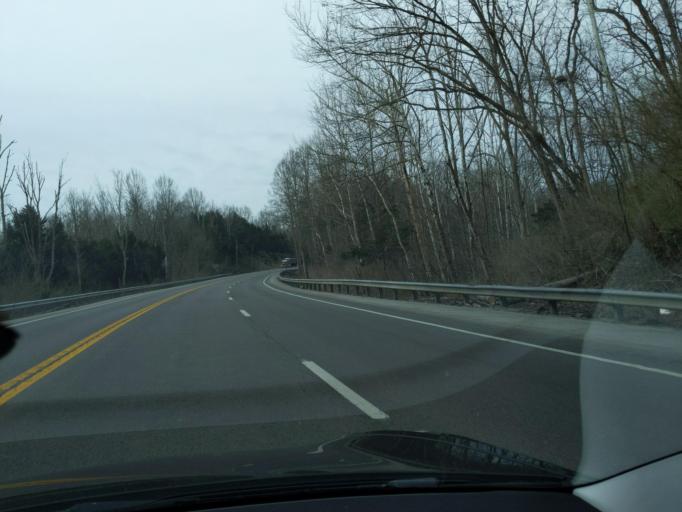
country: US
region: Kentucky
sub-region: Clark County
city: Winchester
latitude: 37.8977
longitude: -84.2705
